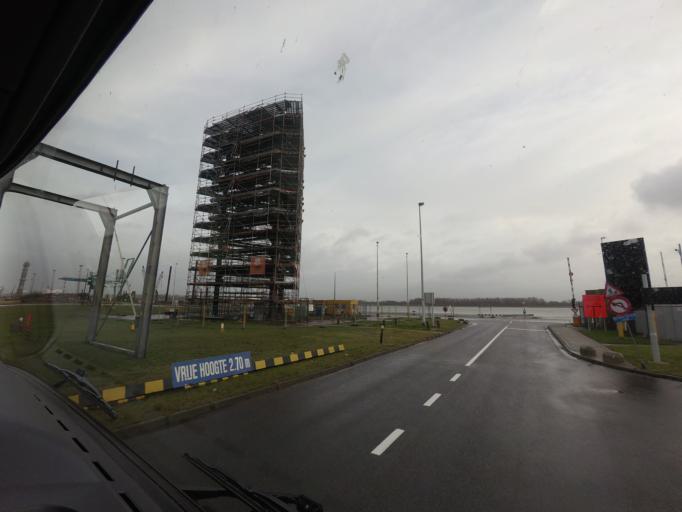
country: BE
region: Flanders
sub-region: Provincie Antwerpen
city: Stabroek
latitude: 51.3465
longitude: 4.2896
